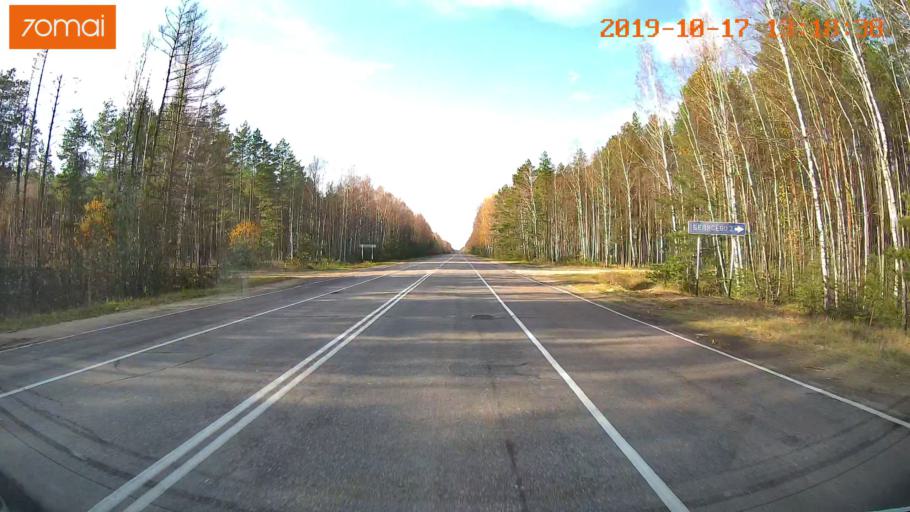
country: RU
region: Rjazan
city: Gus'-Zheleznyy
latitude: 55.0643
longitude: 41.0931
